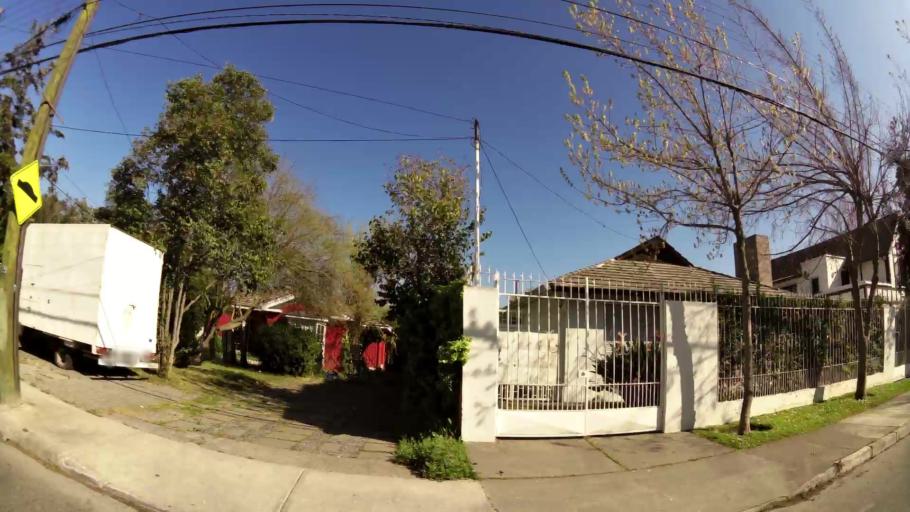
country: CL
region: Santiago Metropolitan
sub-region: Provincia de Santiago
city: Villa Presidente Frei, Nunoa, Santiago, Chile
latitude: -33.4407
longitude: -70.5868
